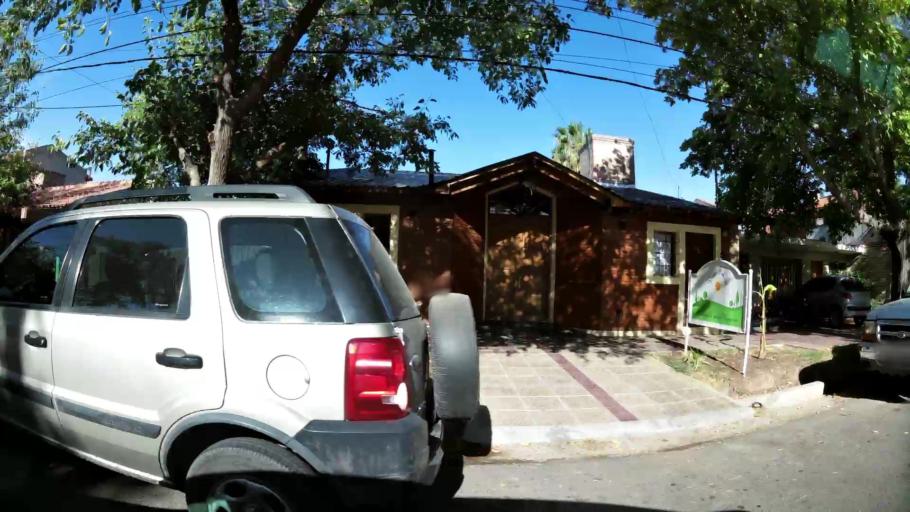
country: AR
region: Mendoza
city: Mendoza
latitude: -32.9098
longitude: -68.8241
